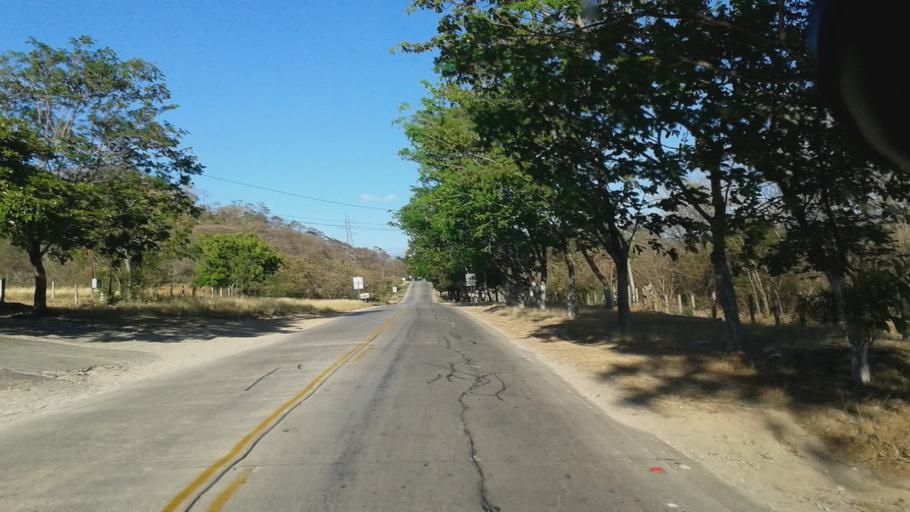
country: CR
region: Guanacaste
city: Nandayure
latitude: 10.2244
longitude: -85.1838
